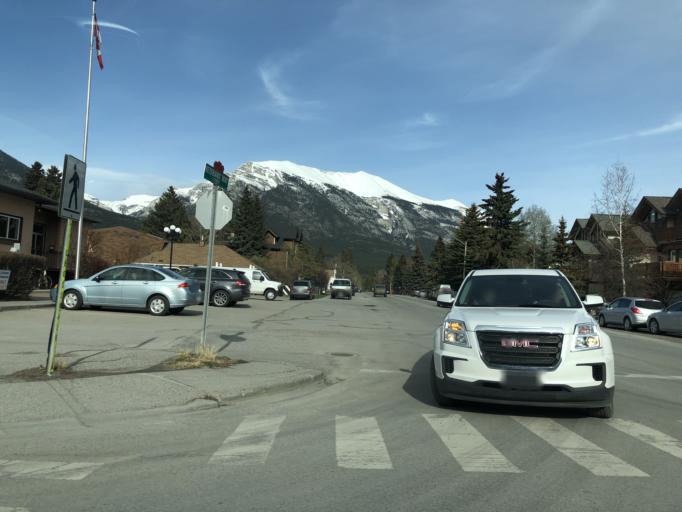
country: CA
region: Alberta
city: Canmore
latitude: 51.0883
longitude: -115.3633
